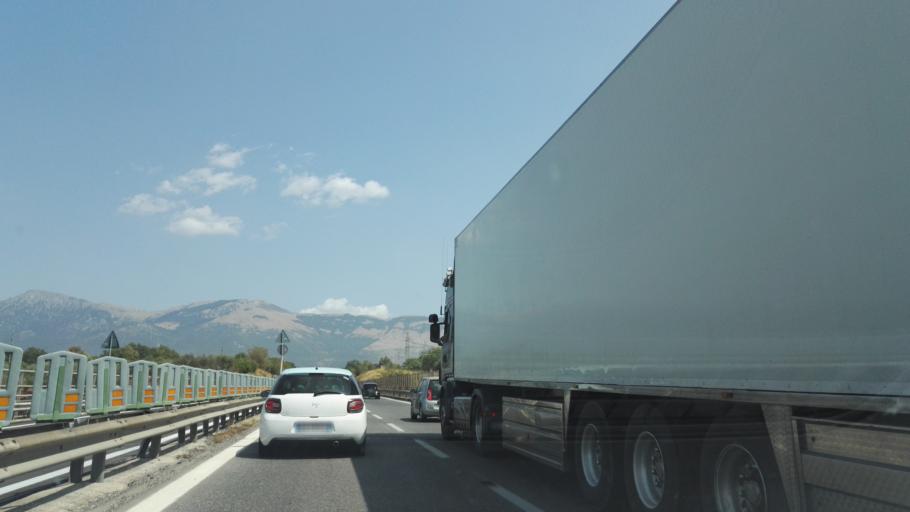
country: IT
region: Calabria
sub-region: Provincia di Cosenza
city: Castrovillari
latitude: 39.7823
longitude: 16.2246
